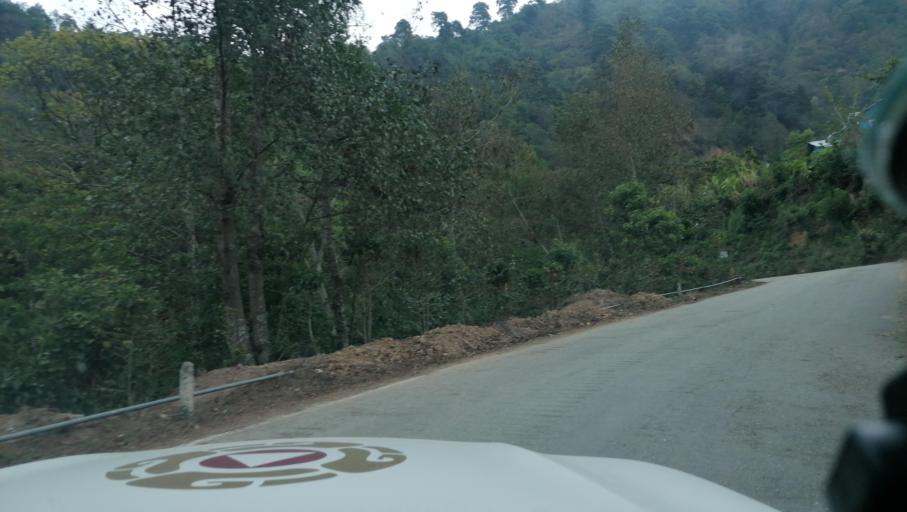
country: GT
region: San Marcos
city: Tacana
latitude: 15.2129
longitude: -92.1994
